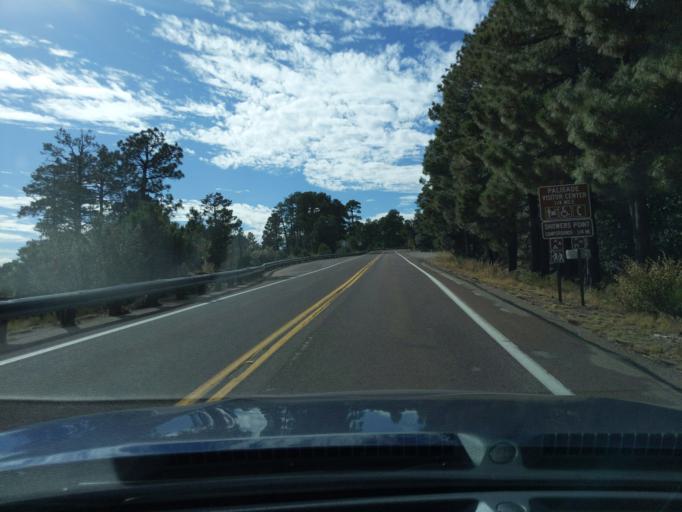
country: US
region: Arizona
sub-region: Pima County
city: Tanque Verde
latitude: 32.4089
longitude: -110.7101
